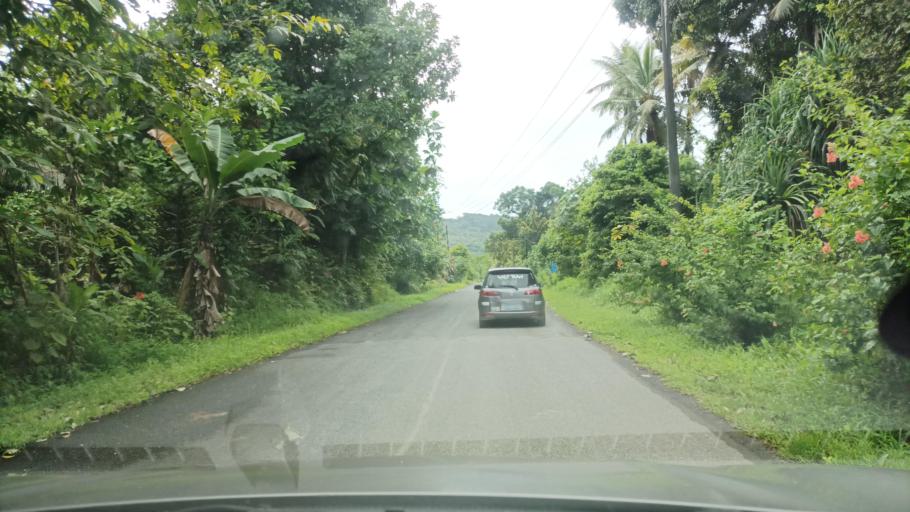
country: FM
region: Pohnpei
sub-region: Kolonia Municipality
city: Kolonia
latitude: 6.9371
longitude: 158.2786
